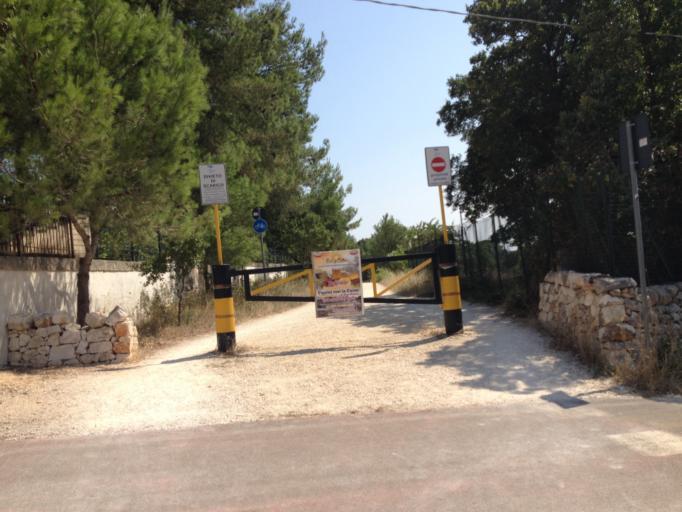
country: IT
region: Apulia
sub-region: Provincia di Brindisi
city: Cisternino
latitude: 40.7137
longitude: 17.4078
